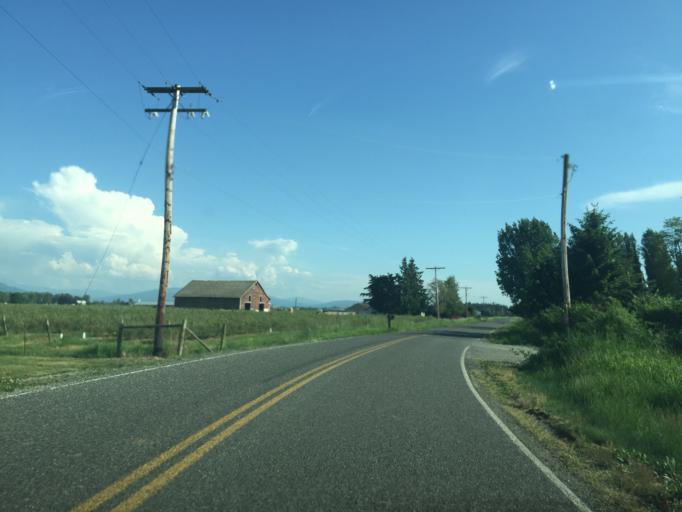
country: US
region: Washington
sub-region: Whatcom County
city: Lynden
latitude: 48.9936
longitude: -122.4628
